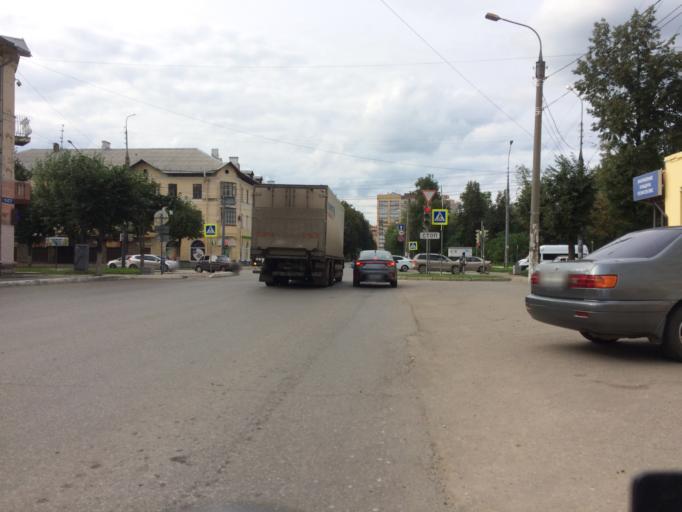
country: RU
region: Mariy-El
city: Yoshkar-Ola
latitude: 56.6376
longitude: 47.8680
